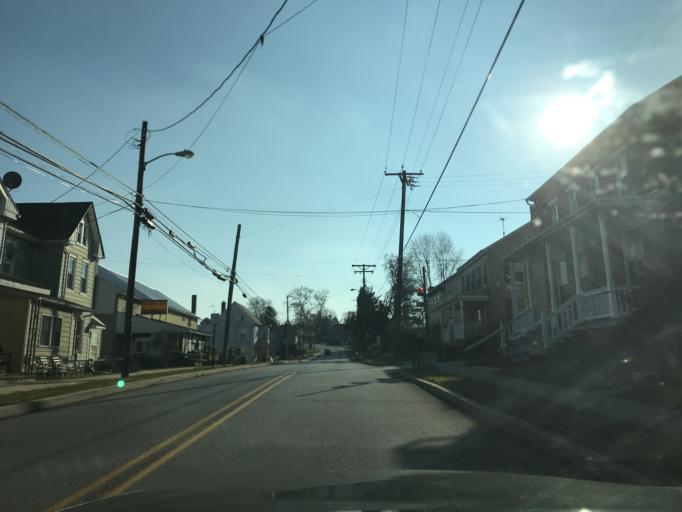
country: US
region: Pennsylvania
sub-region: York County
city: Loganville
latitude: 39.8490
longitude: -76.7104
